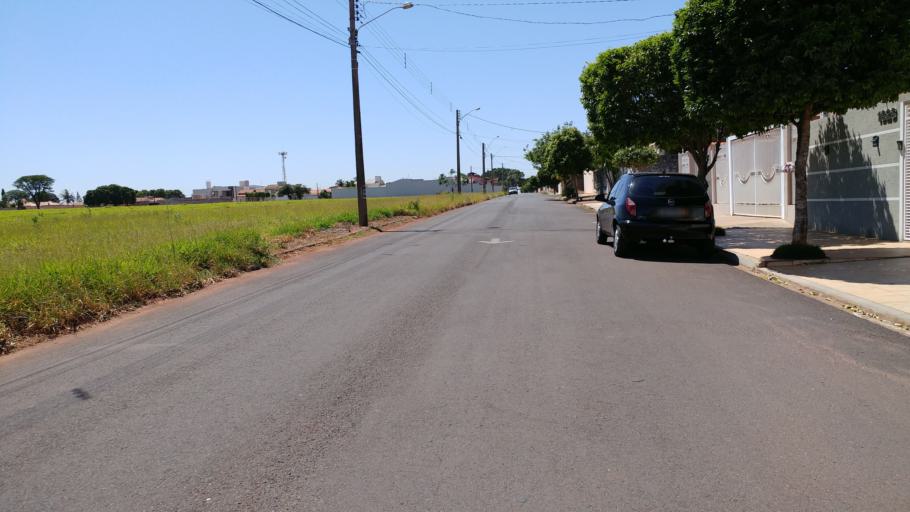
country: BR
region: Sao Paulo
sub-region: Paraguacu Paulista
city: Paraguacu Paulista
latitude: -22.4099
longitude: -50.5861
